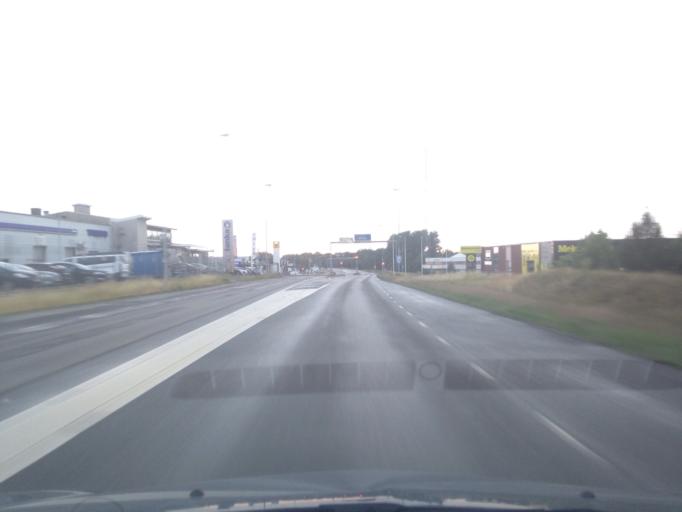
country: SE
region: Halland
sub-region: Varbergs Kommun
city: Varberg
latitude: 57.1234
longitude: 12.2799
